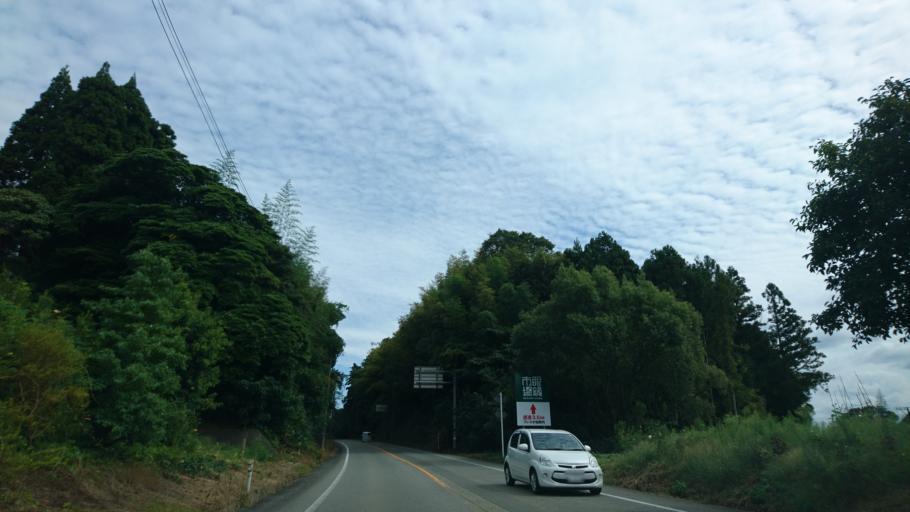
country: JP
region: Ishikawa
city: Komatsu
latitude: 36.3137
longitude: 136.3180
